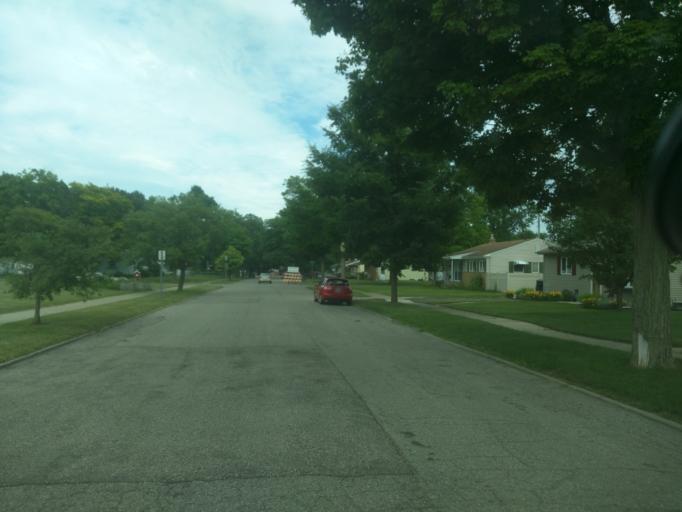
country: US
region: Michigan
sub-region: Ingham County
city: Lansing
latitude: 42.6861
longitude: -84.5405
